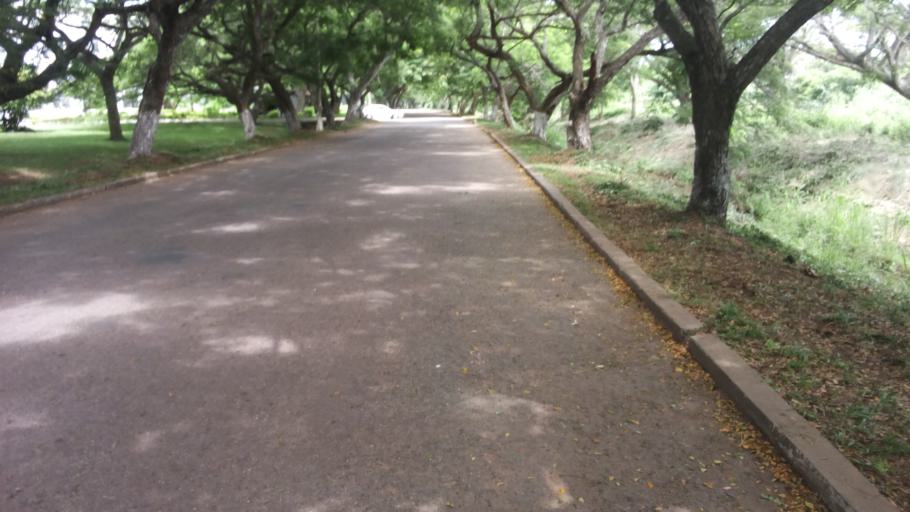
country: GH
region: Central
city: Cape Coast
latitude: 5.1217
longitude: -1.2862
